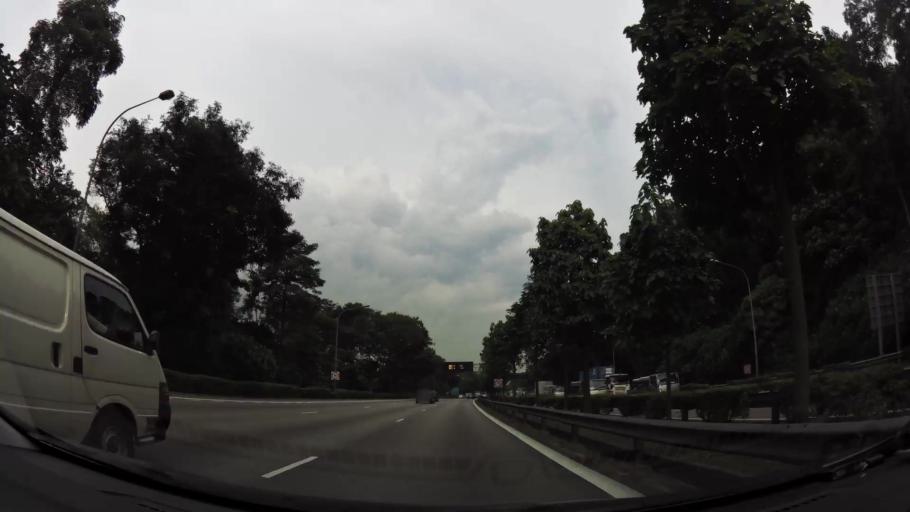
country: MY
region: Johor
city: Johor Bahru
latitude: 1.4252
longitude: 103.7764
